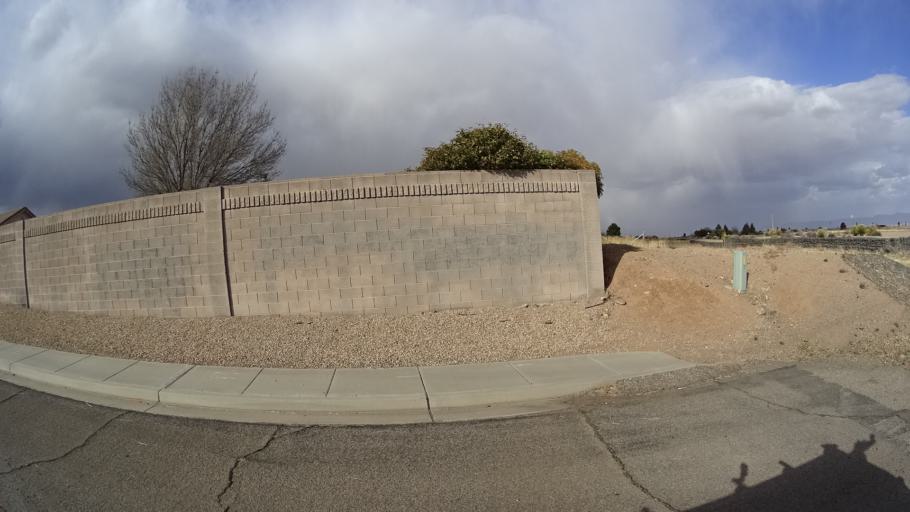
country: US
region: Arizona
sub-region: Mohave County
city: New Kingman-Butler
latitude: 35.2323
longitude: -114.0287
